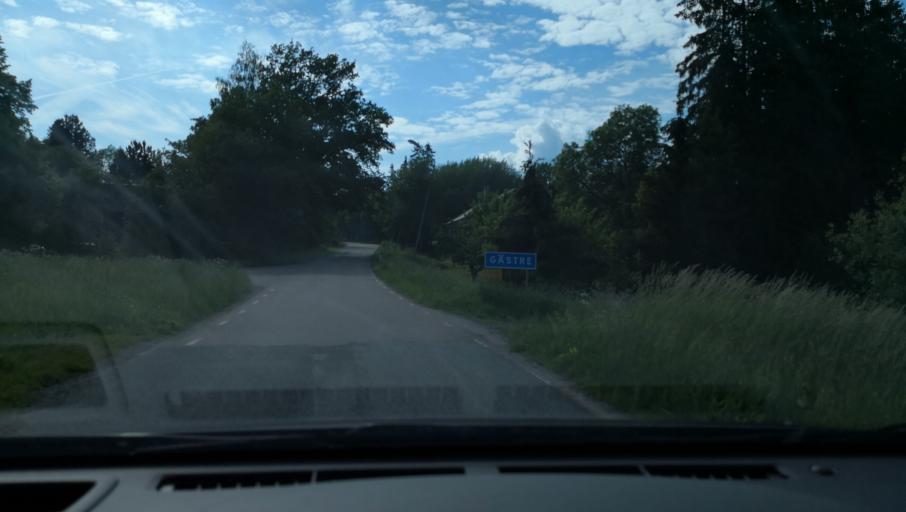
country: SE
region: Uppsala
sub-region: Enkopings Kommun
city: Irsta
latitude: 59.7536
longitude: 16.9519
